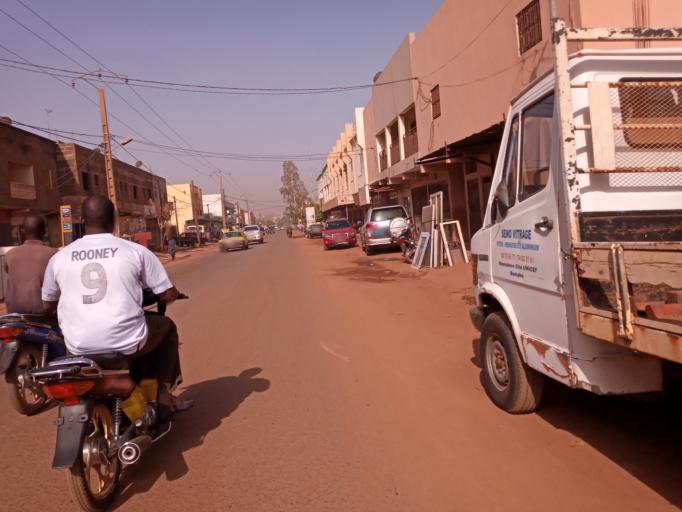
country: ML
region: Bamako
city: Bamako
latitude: 12.5884
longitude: -7.9736
